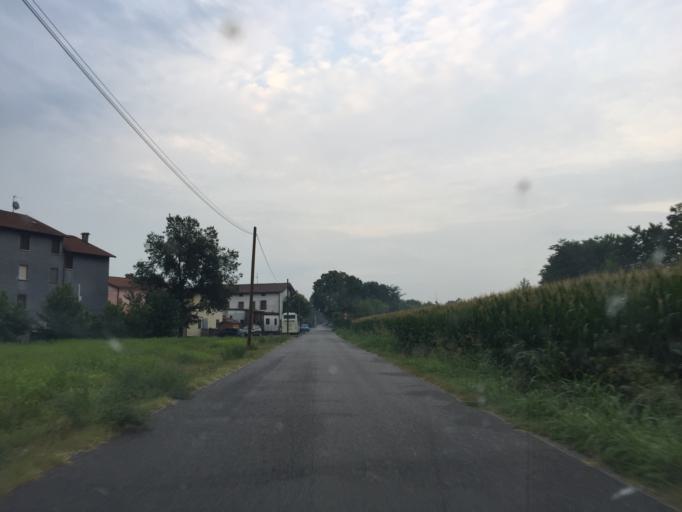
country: IT
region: Lombardy
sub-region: Provincia di Brescia
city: Flero
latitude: 45.4901
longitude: 10.1752
